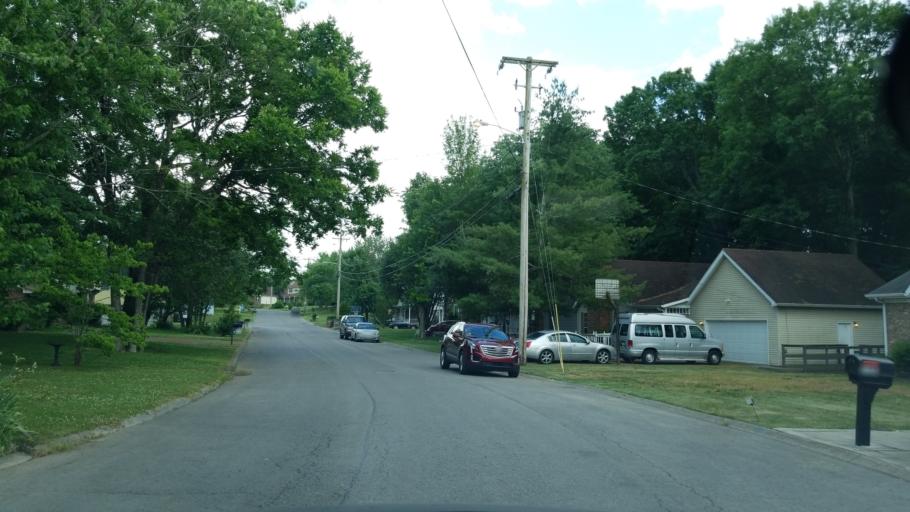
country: US
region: Tennessee
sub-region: Rutherford County
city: La Vergne
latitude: 36.0739
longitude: -86.6054
